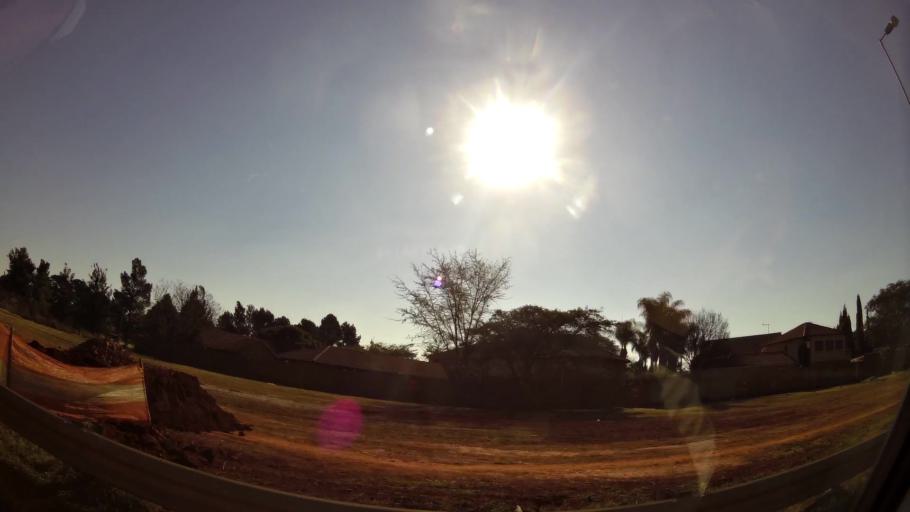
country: ZA
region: Gauteng
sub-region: City of Tshwane Metropolitan Municipality
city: Centurion
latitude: -25.8377
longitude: 28.2849
